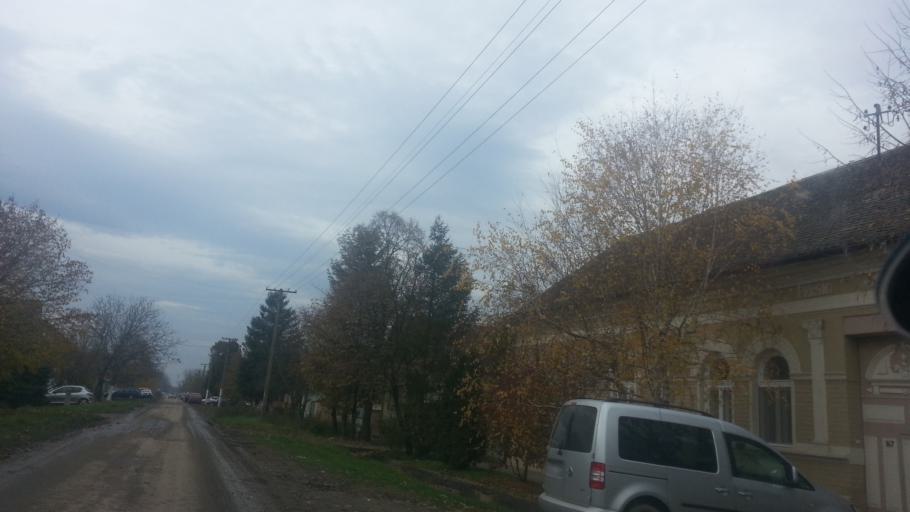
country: RS
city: Golubinci
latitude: 44.9862
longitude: 20.0797
